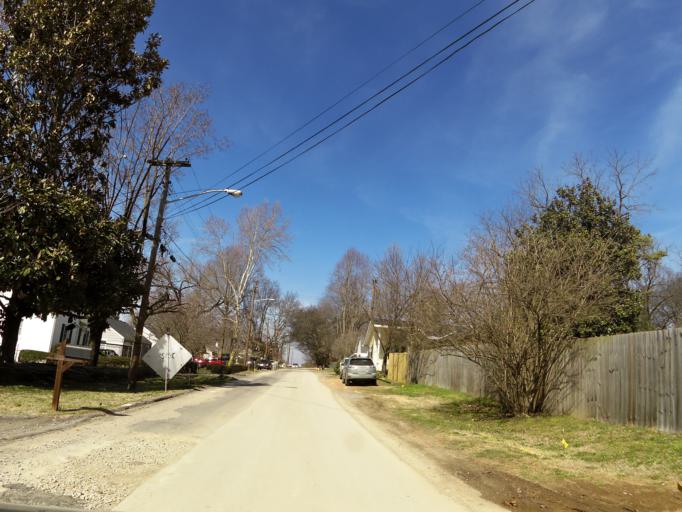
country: US
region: Tennessee
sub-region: Davidson County
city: Belle Meade
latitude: 36.1463
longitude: -86.8509
